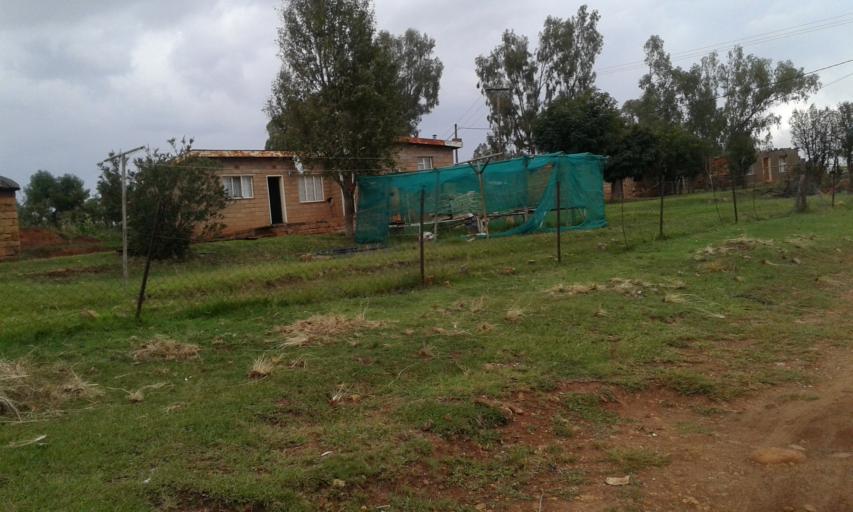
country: LS
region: Maseru
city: Maseru
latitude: -29.4254
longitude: 27.5741
